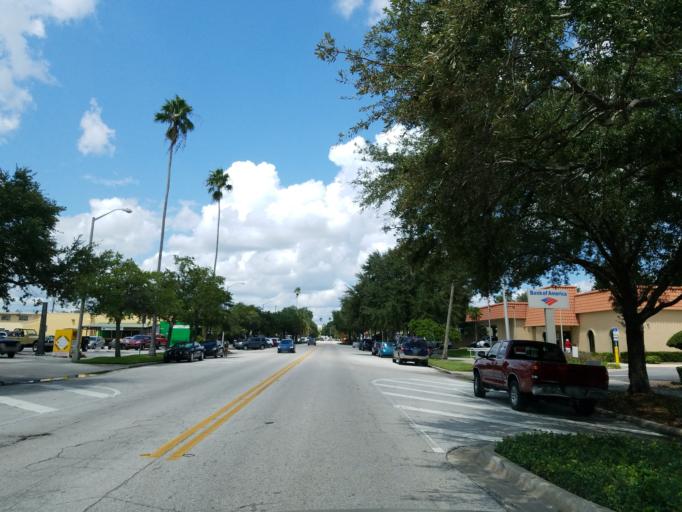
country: US
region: Florida
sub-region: Hillsborough County
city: Tampa
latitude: 27.9248
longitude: -82.4524
